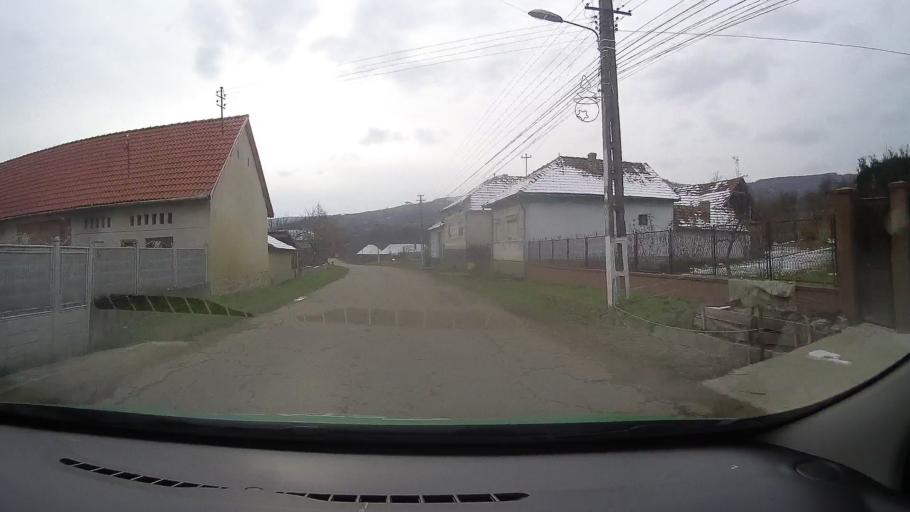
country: RO
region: Hunedoara
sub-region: Comuna Geoagiu
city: Geoagiu
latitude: 45.9695
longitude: 23.1699
